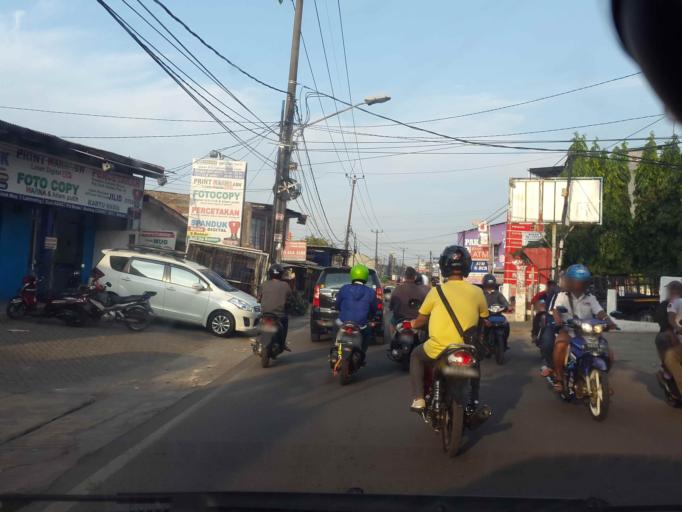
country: ID
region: Banten
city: South Tangerang
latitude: -6.2614
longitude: 106.7386
